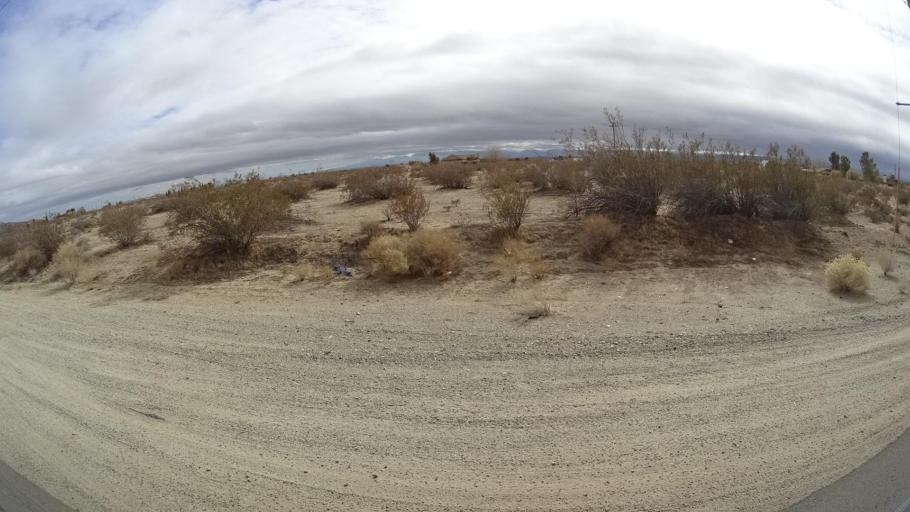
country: US
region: California
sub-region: Kern County
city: Rosamond
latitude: 34.8756
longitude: -118.2272
